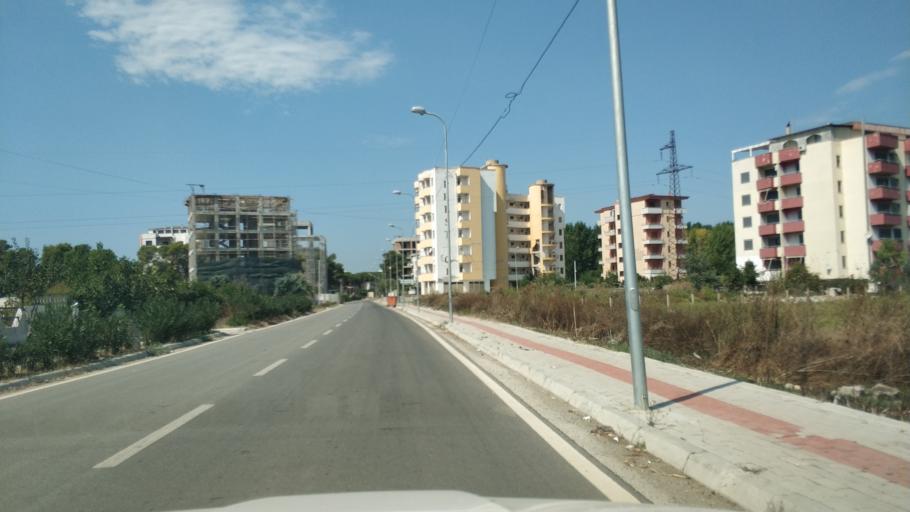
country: AL
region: Tirane
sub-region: Rrethi i Kavajes
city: Golem
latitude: 41.2367
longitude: 19.5229
